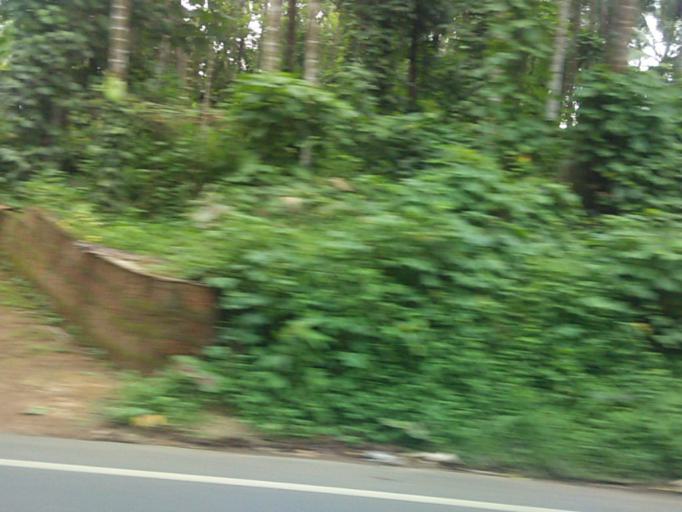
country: IN
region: Kerala
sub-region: Kozhikode
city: Kunnamangalam
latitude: 11.2956
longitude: 75.8429
